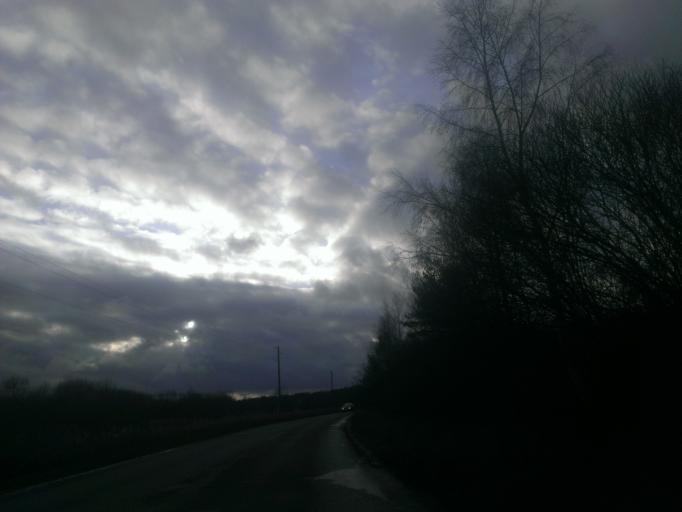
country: LV
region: Riga
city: Bolderaja
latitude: 57.0667
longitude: 24.0871
